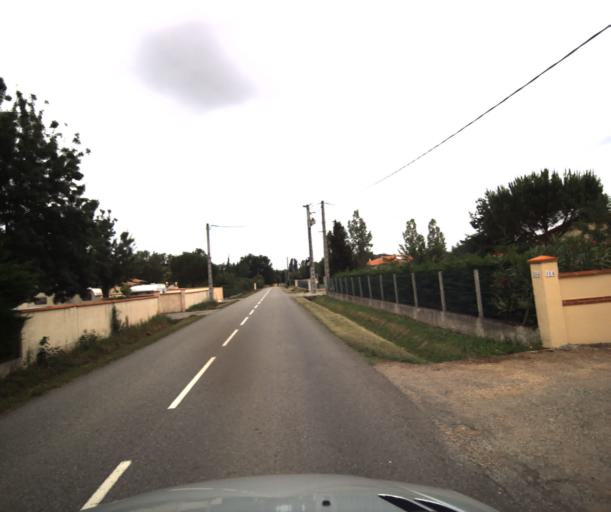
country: FR
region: Midi-Pyrenees
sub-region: Departement de la Haute-Garonne
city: Labarthe-sur-Leze
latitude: 43.4530
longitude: 1.4099
